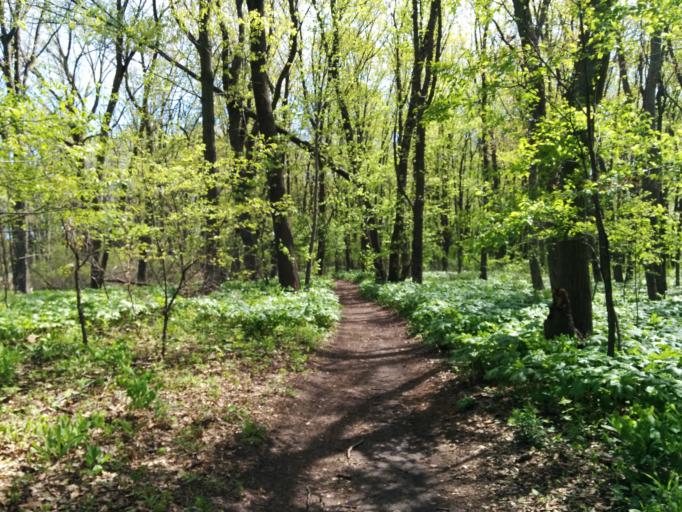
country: US
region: Indiana
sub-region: Lake County
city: Whiting
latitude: 41.6835
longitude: -87.5296
